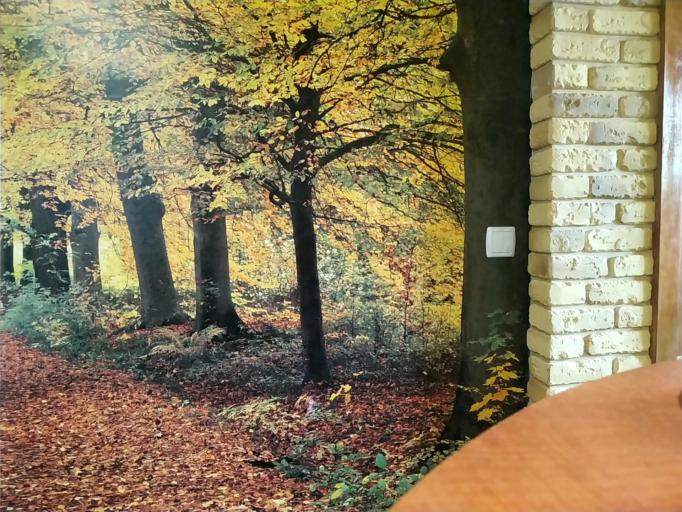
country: RU
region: Novgorod
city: Opechenskiy Posad
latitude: 58.2684
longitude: 34.0201
